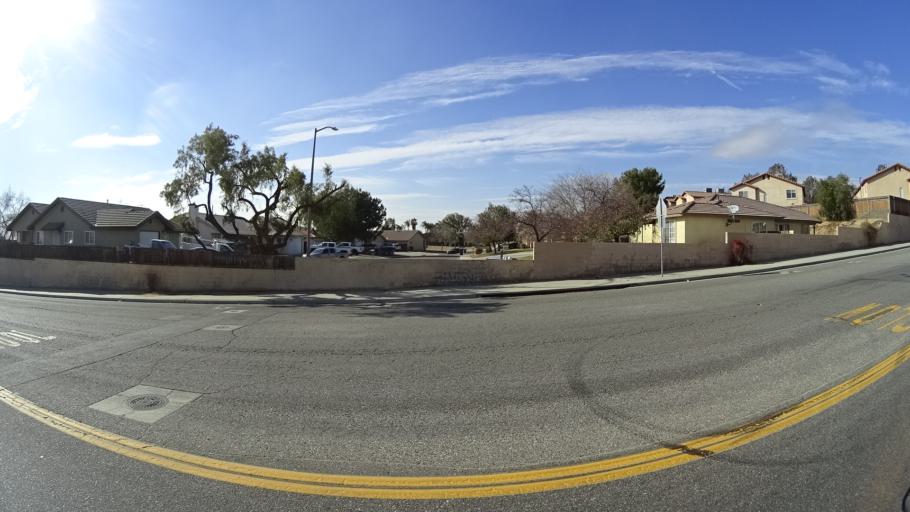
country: US
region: California
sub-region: Kern County
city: Bakersfield
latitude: 35.3811
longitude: -118.9144
